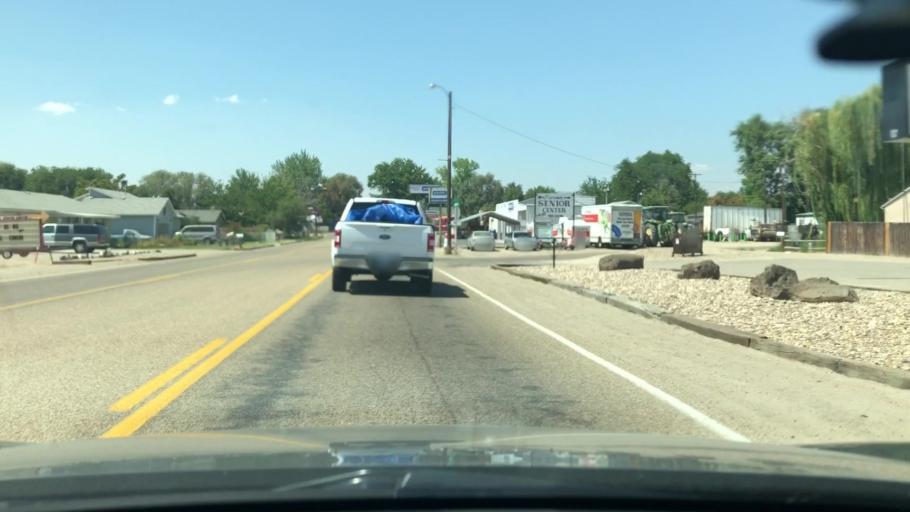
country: US
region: Idaho
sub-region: Canyon County
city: Parma
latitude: 43.7817
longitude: -116.9369
